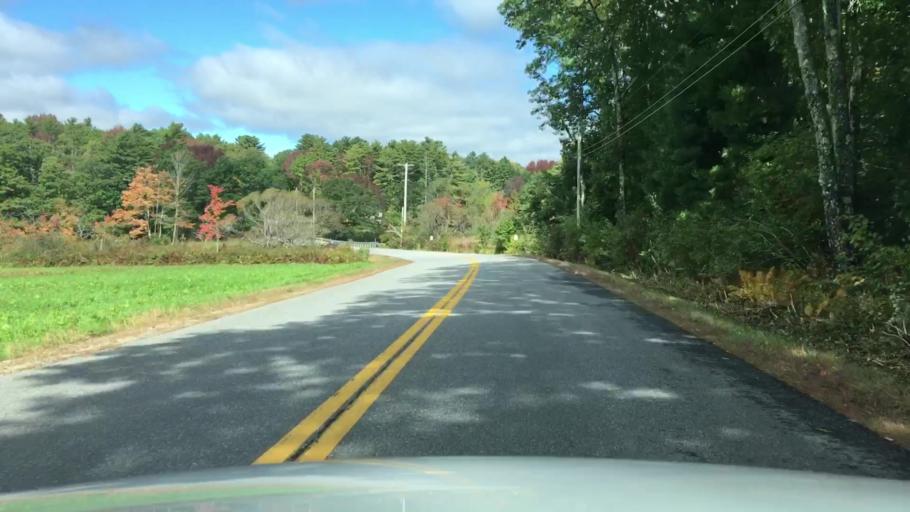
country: US
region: Maine
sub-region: Cumberland County
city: Brunswick
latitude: 43.9638
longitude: -69.8964
